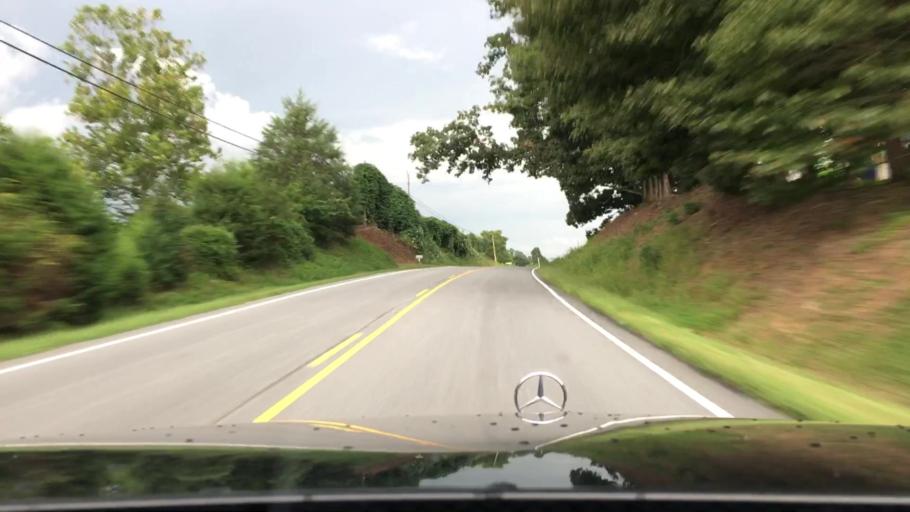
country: US
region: Virginia
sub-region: Nelson County
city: Lovingston
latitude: 37.7893
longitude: -78.9759
